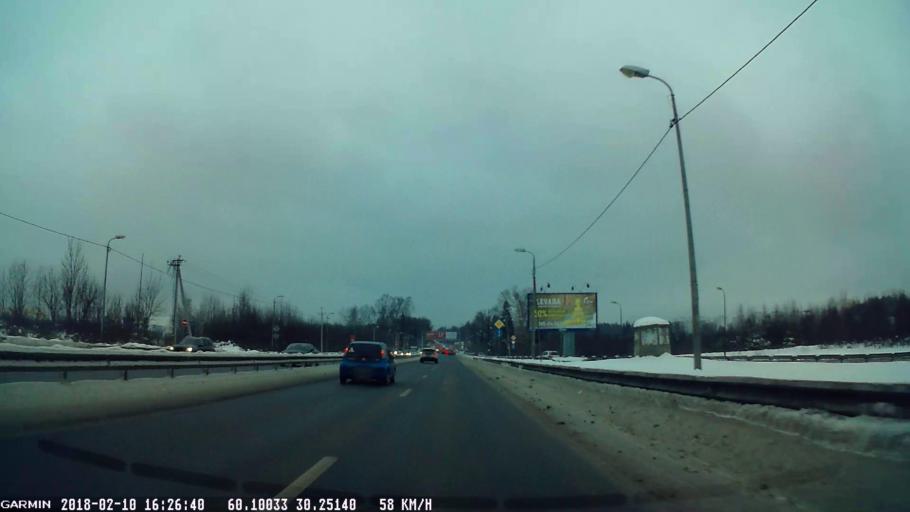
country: RU
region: St.-Petersburg
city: Pargolovo
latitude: 60.1005
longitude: 30.2513
